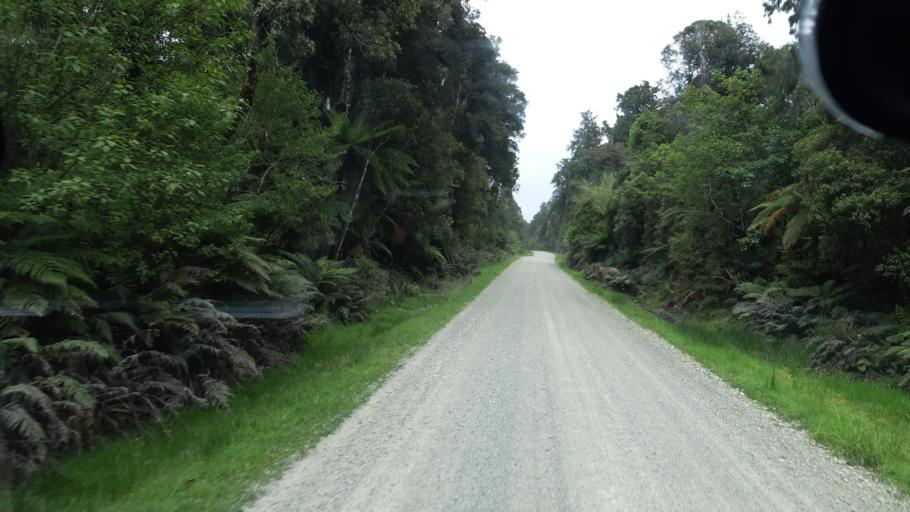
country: NZ
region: West Coast
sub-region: Grey District
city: Greymouth
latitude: -42.6470
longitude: 171.3323
